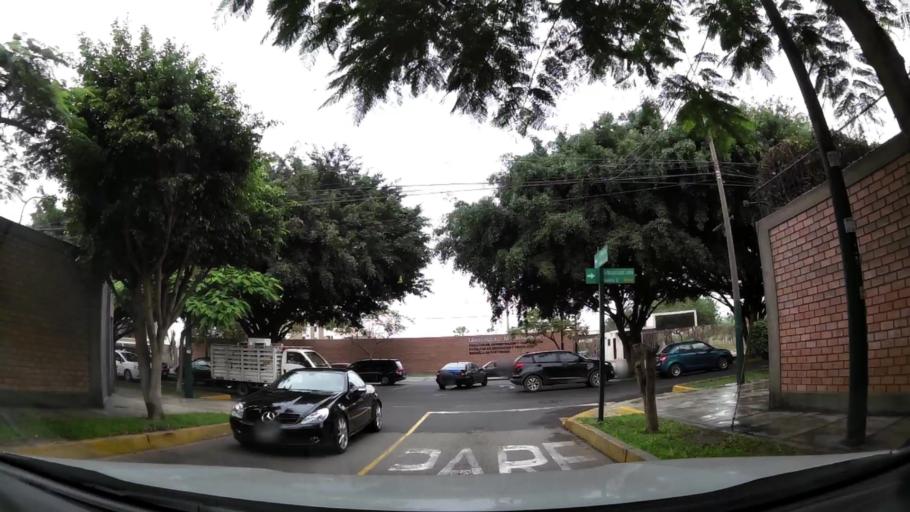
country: PE
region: Lima
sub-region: Lima
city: Surco
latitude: -12.1361
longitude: -77.0056
